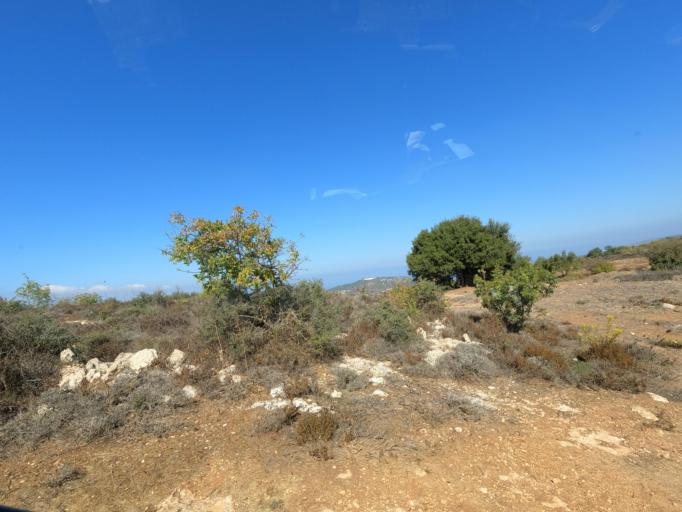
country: CY
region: Pafos
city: Polis
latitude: 34.9819
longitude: 32.5042
